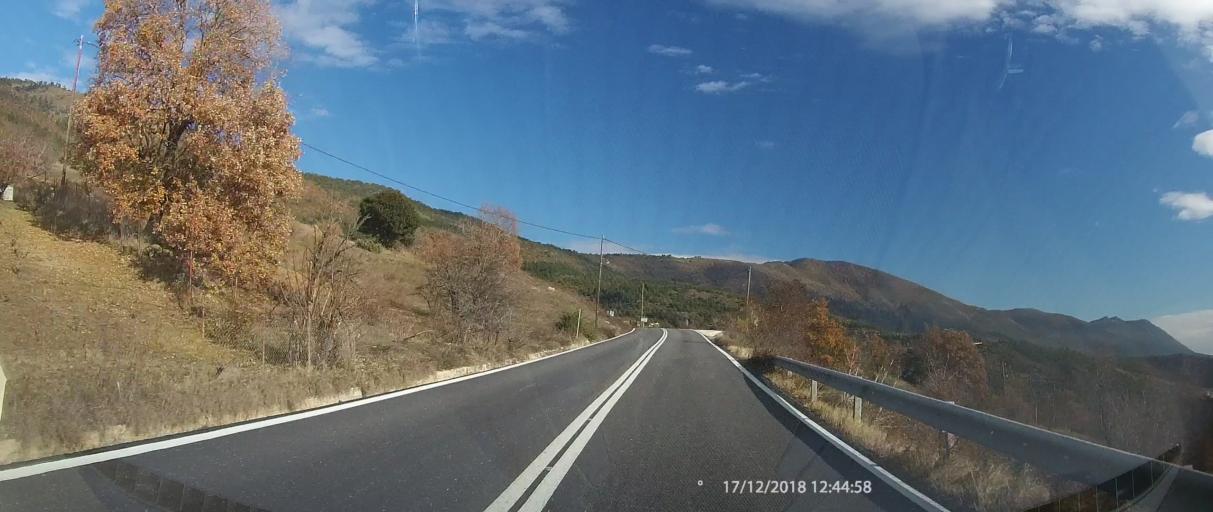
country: GR
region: Thessaly
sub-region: Trikala
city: Kastraki
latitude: 39.7854
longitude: 21.4056
